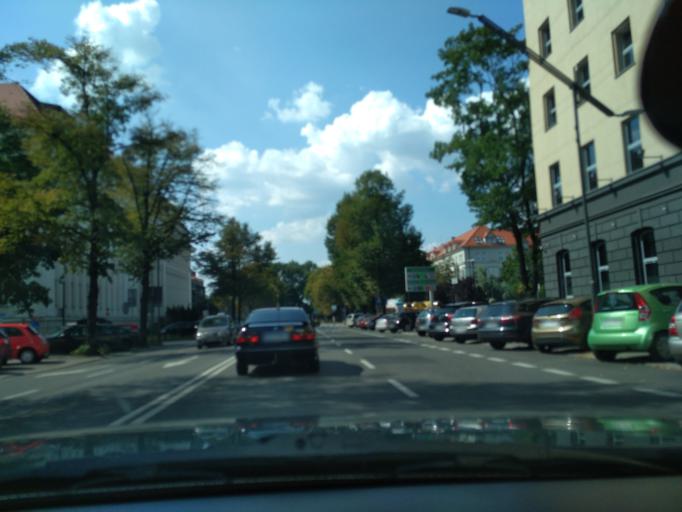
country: PL
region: Silesian Voivodeship
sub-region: Gliwice
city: Gliwice
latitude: 50.2962
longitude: 18.6687
